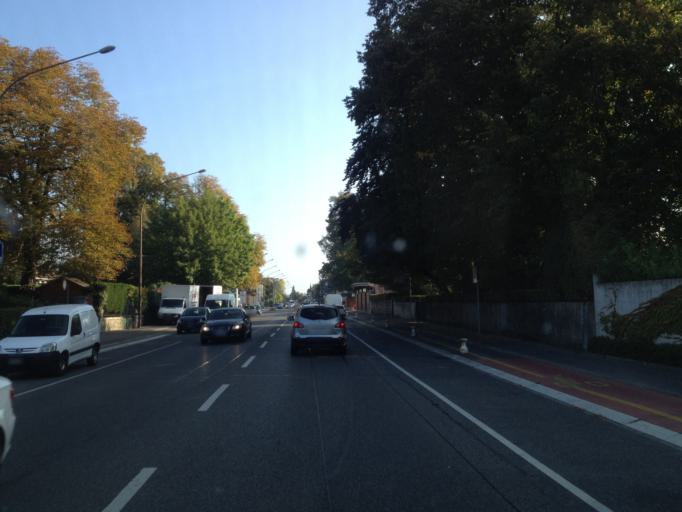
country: CH
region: Geneva
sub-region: Geneva
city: Bellevue
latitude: 46.2528
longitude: 6.1525
